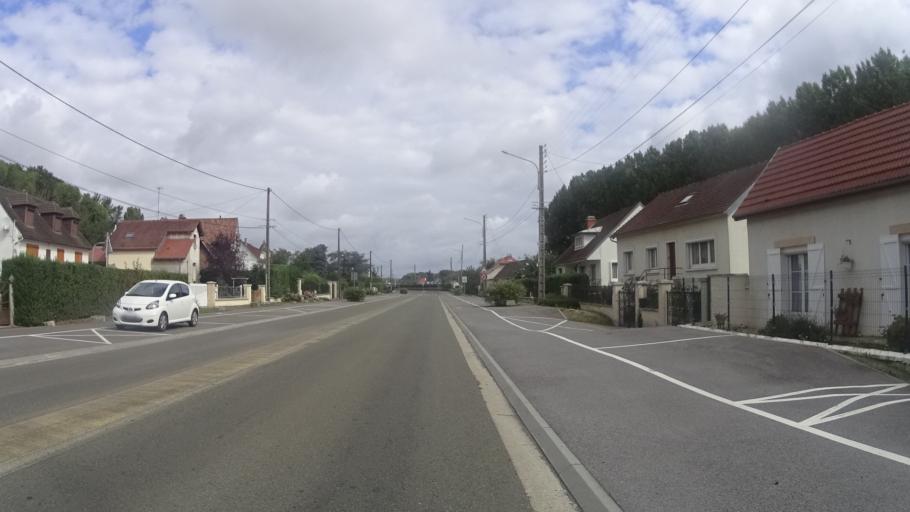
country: FR
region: Picardie
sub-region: Departement de l'Oise
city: Choisy-au-Bac
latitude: 49.4489
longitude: 2.8647
